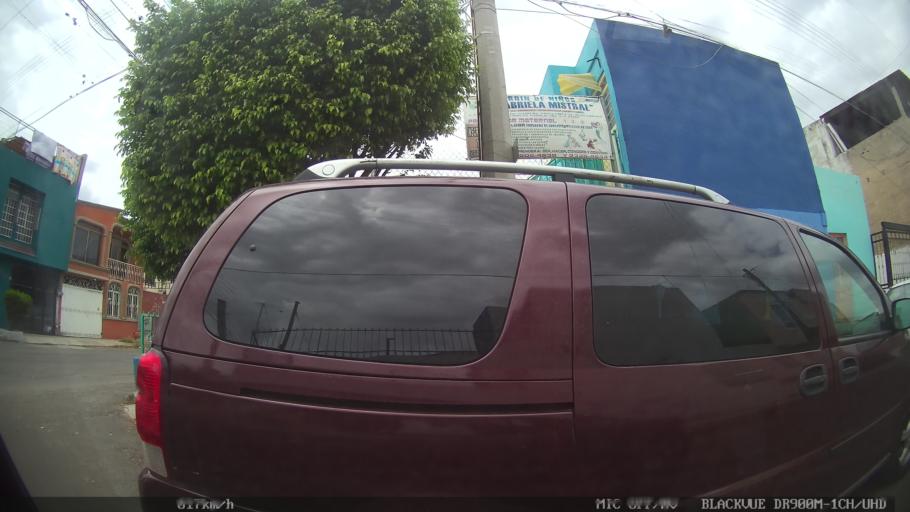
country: MX
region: Jalisco
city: Tonala
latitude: 20.6395
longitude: -103.2537
